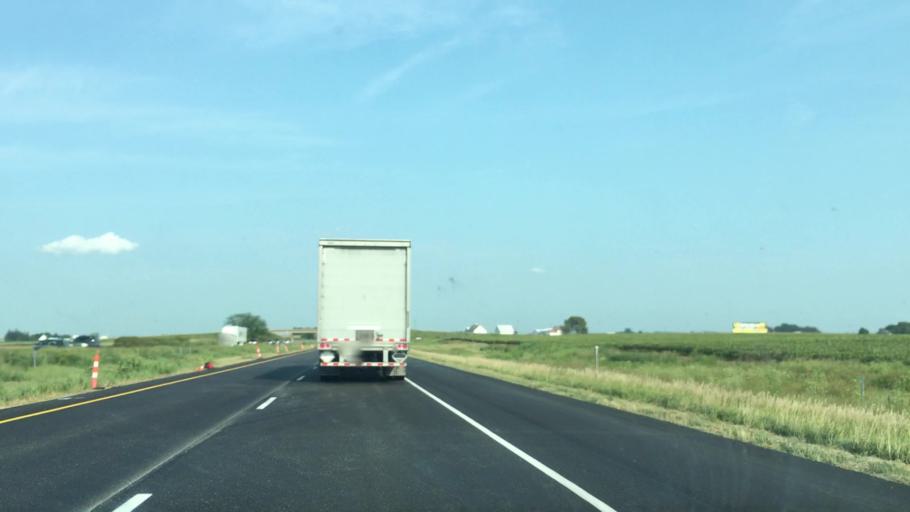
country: US
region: Iowa
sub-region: Scott County
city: Walcott
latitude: 41.6097
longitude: -90.7499
